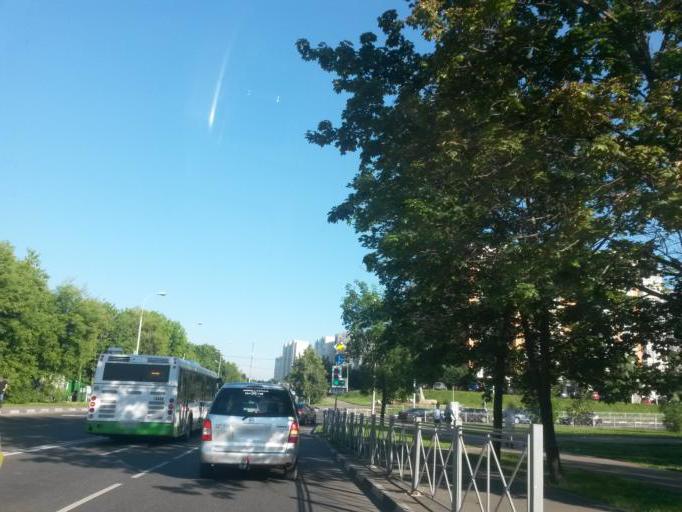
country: RU
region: Moscow
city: Zyablikovo
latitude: 55.6248
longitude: 37.7532
